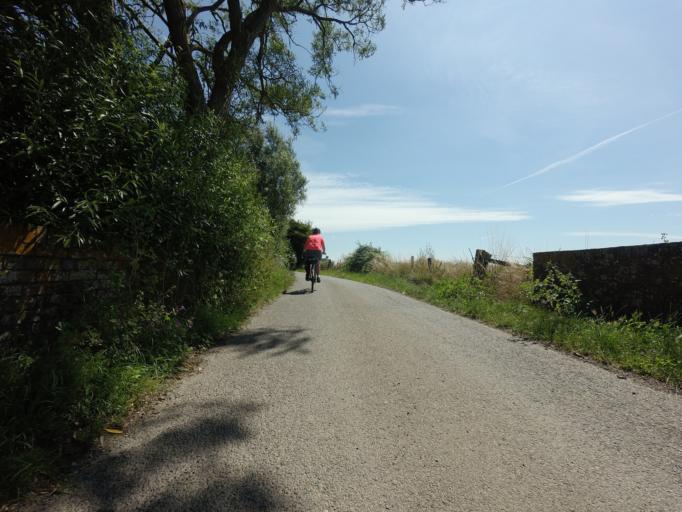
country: GB
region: England
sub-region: Kent
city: Lydd
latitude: 50.9855
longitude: 0.8737
